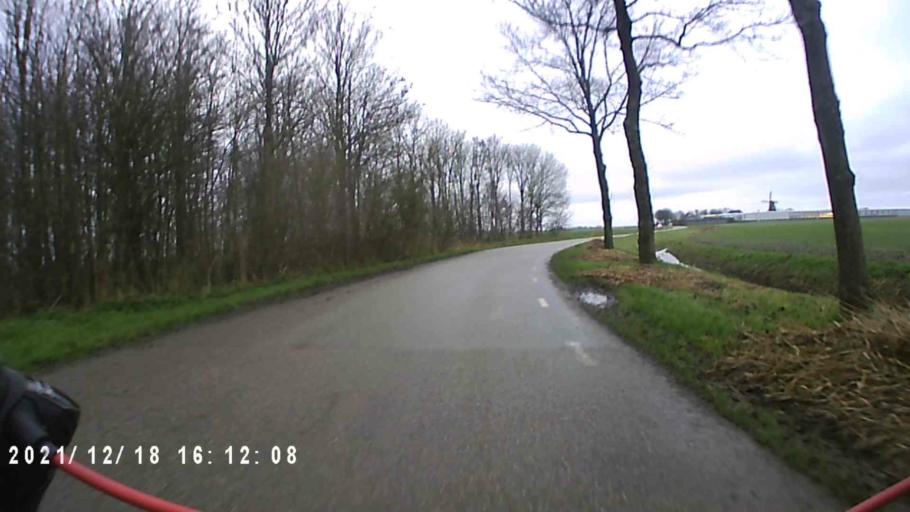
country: NL
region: Friesland
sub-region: Gemeente Dongeradeel
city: Anjum
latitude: 53.3643
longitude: 6.0685
